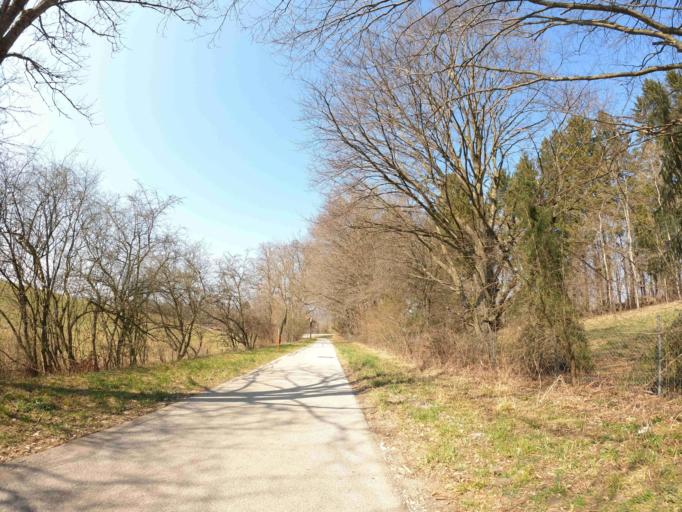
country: DE
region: Bavaria
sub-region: Upper Bavaria
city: Starnberg
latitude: 47.9997
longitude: 11.3715
